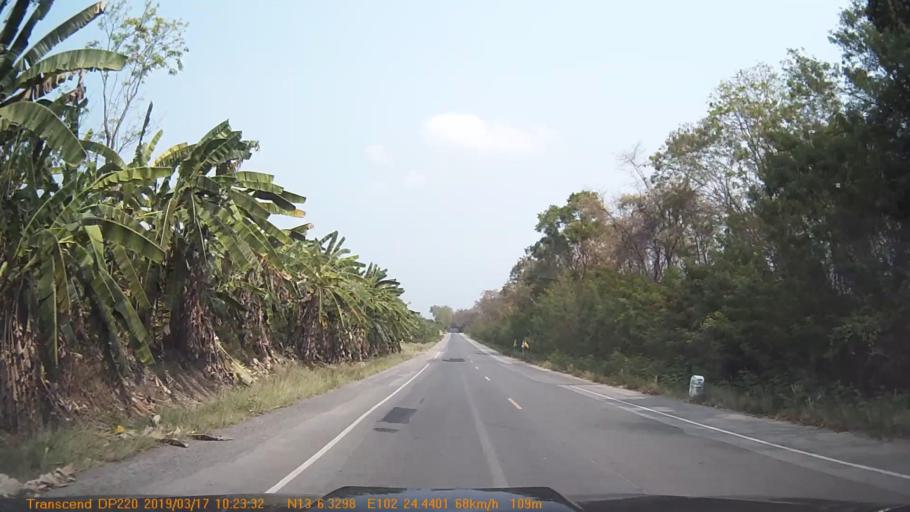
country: TH
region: Chanthaburi
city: Soi Dao
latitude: 13.1057
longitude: 102.4073
